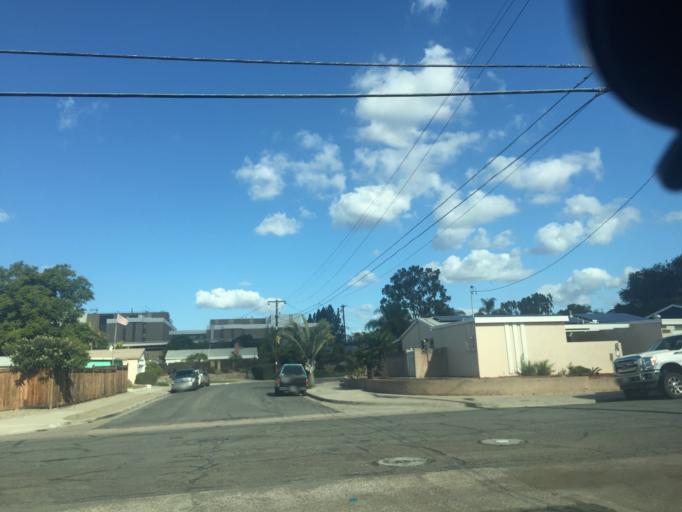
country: US
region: California
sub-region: San Diego County
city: La Mesa
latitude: 32.7885
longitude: -117.0948
